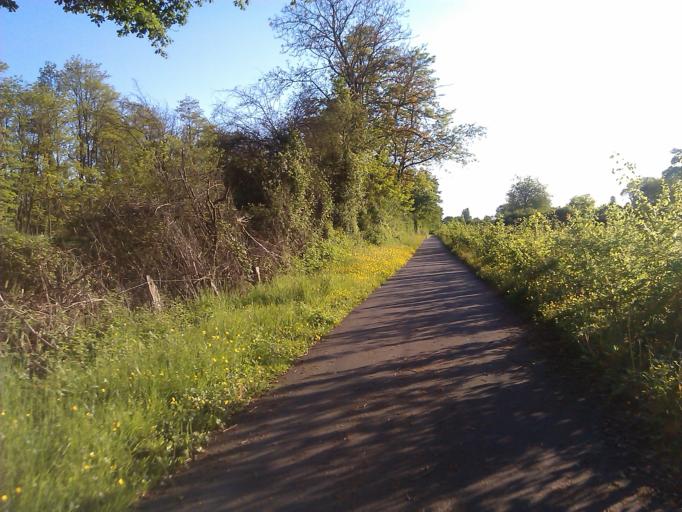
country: FR
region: Auvergne
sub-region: Departement de l'Allier
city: Dompierre-sur-Besbre
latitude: 46.5333
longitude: 3.7015
